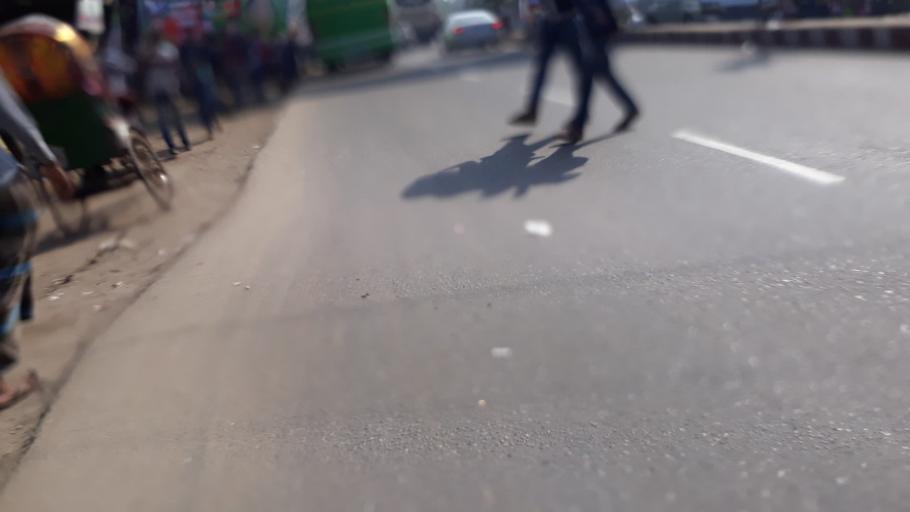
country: BD
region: Dhaka
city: Tungi
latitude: 23.8960
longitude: 90.2709
